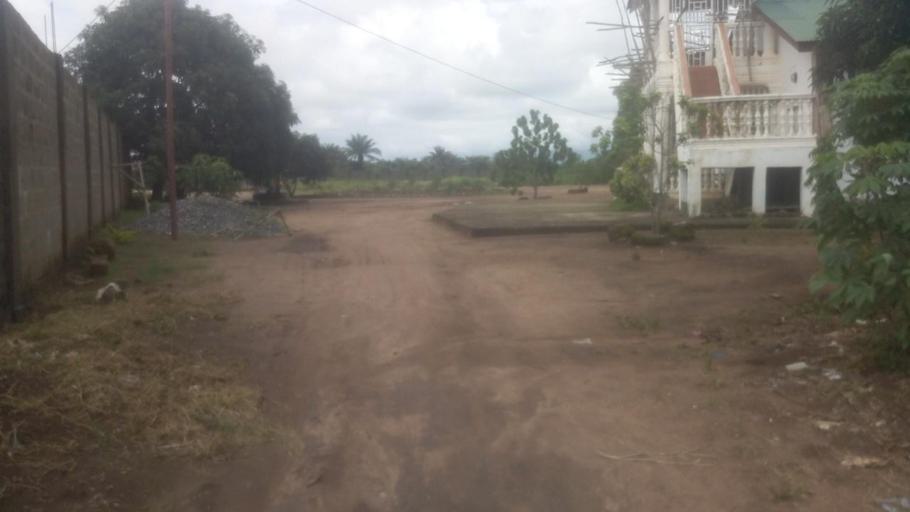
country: SL
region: Northern Province
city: Masoyila
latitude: 8.5935
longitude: -13.1936
